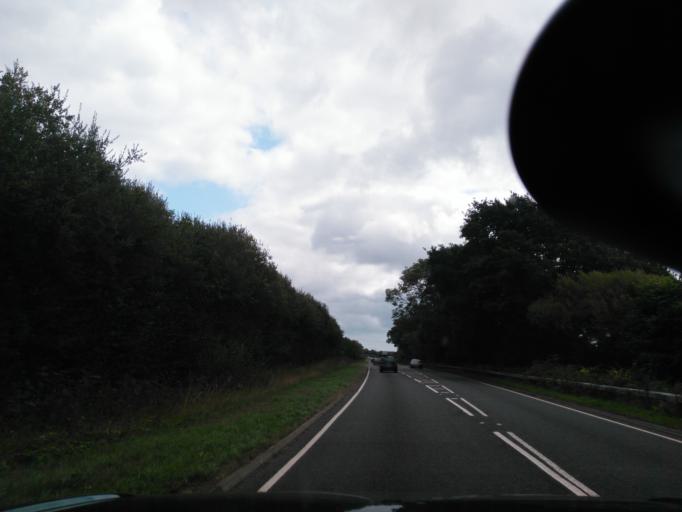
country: GB
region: England
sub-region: Dorset
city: Lytchett Matravers
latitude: 50.7347
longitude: -2.0770
